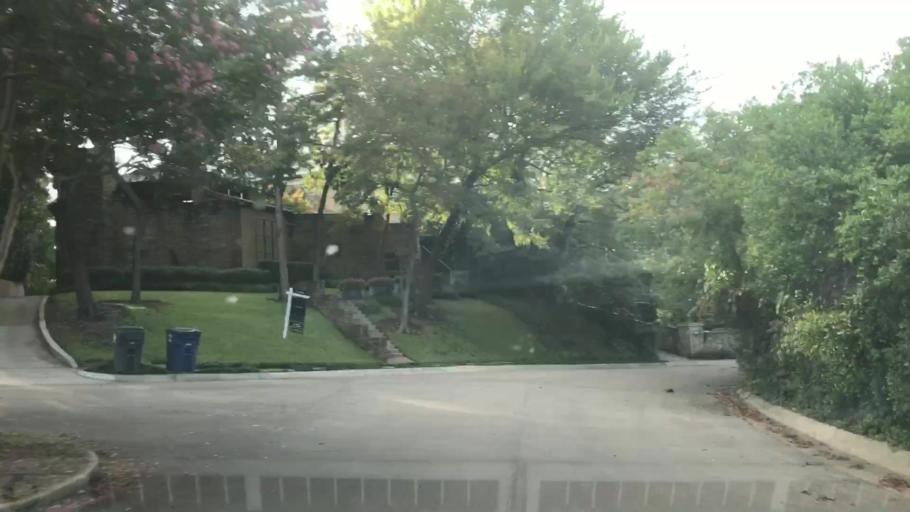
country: US
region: Texas
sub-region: Dallas County
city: Cockrell Hill
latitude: 32.7581
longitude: -96.8470
